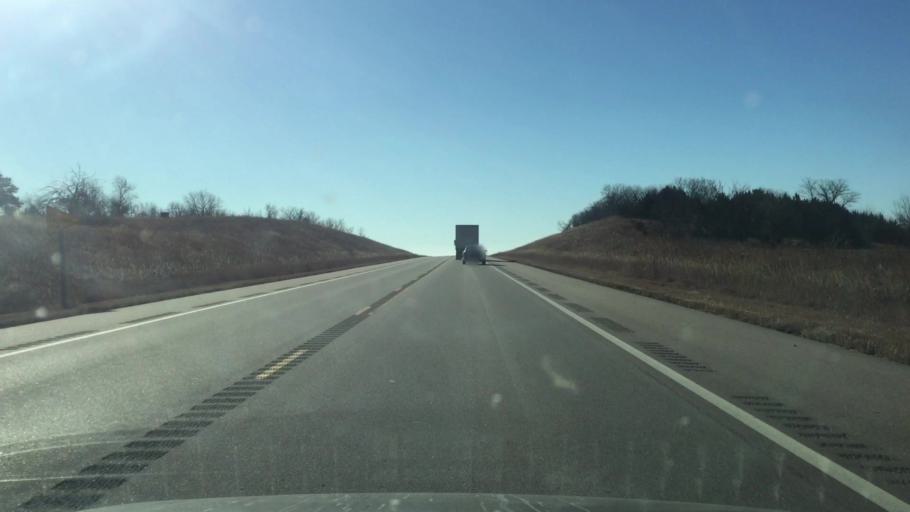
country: US
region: Kansas
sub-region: Allen County
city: Iola
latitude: 38.0144
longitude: -95.3807
